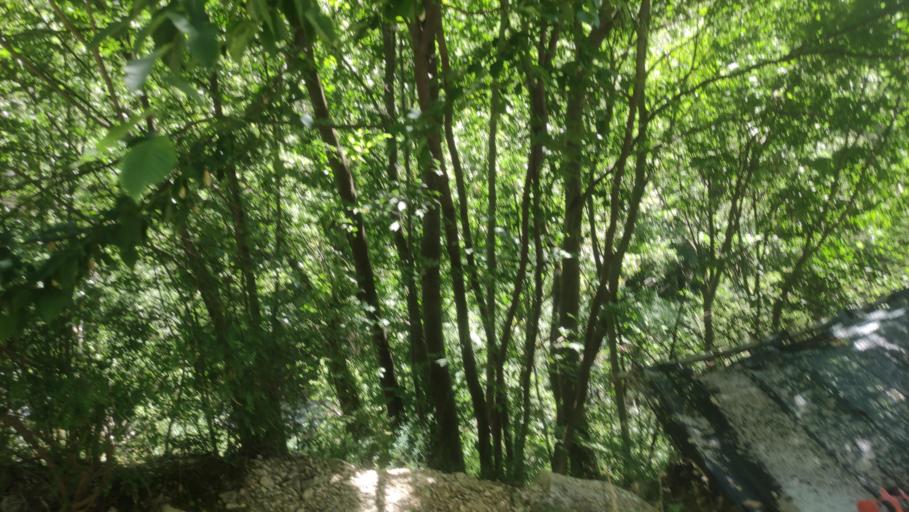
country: IT
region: The Marches
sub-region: Provincia di Ancona
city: Serra San Quirico
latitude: 43.4284
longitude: 13.0019
